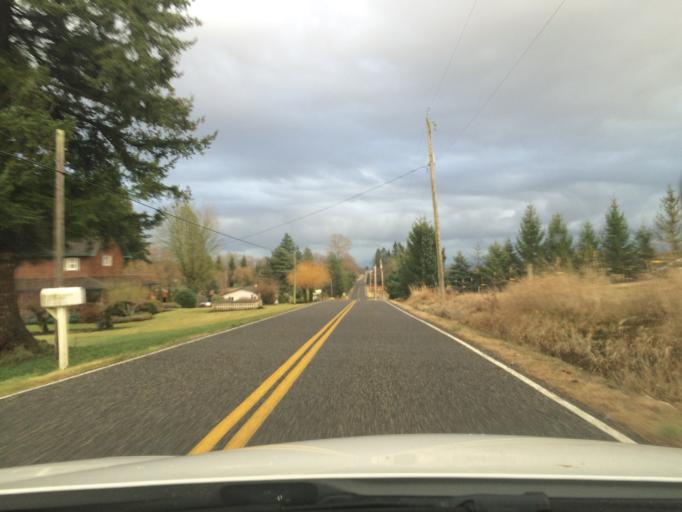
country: CA
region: British Columbia
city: Aldergrove
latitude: 48.9934
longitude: -122.5157
